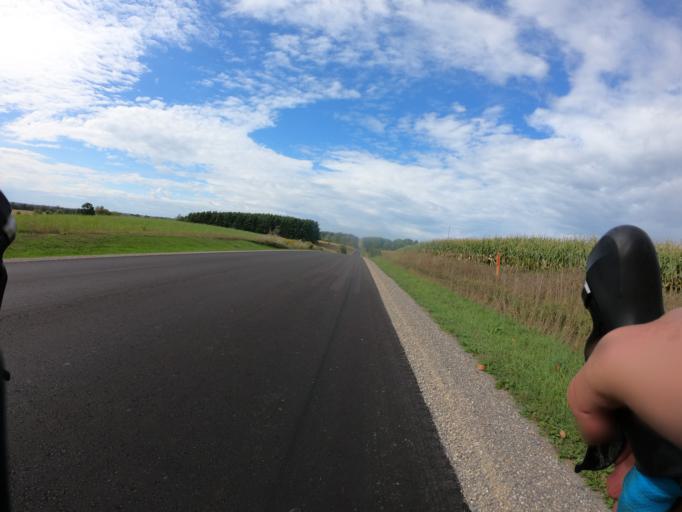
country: CA
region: Ontario
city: Kitchener
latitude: 43.3794
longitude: -80.6206
